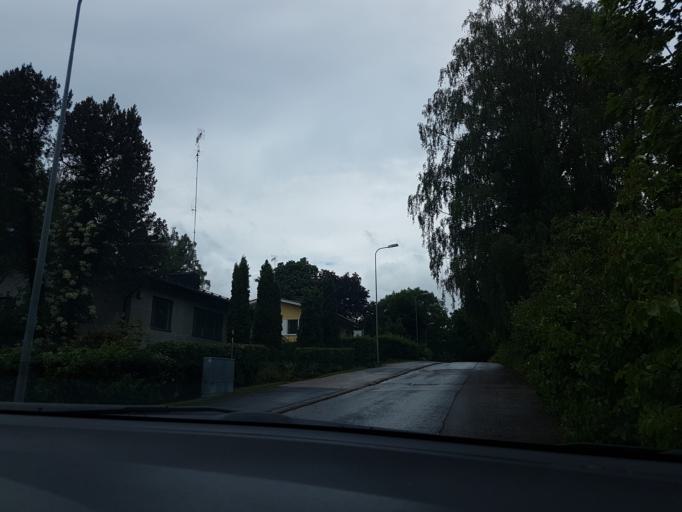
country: FI
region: Uusimaa
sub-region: Helsinki
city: Vantaa
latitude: 60.2294
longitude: 25.1151
